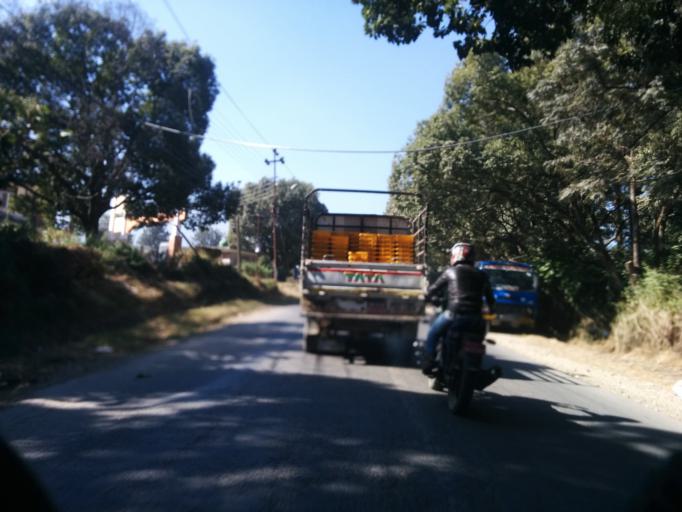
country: NP
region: Central Region
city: Kirtipur
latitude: 27.6788
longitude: 85.2887
